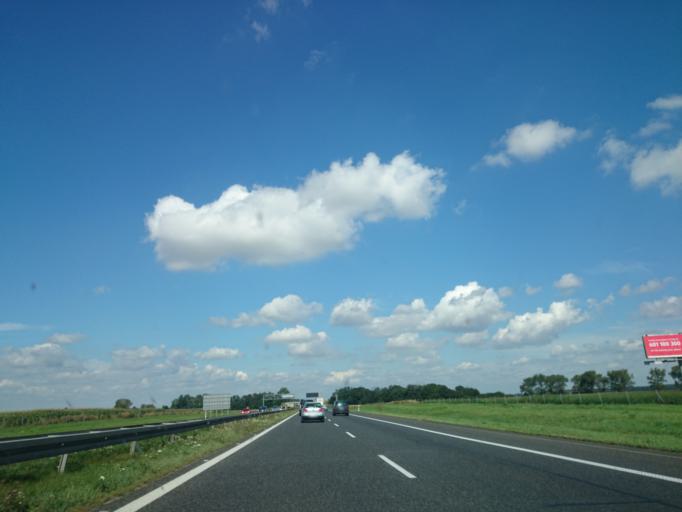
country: PL
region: Lower Silesian Voivodeship
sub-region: Powiat olawski
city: Wierzbno
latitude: 50.8843
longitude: 17.1955
